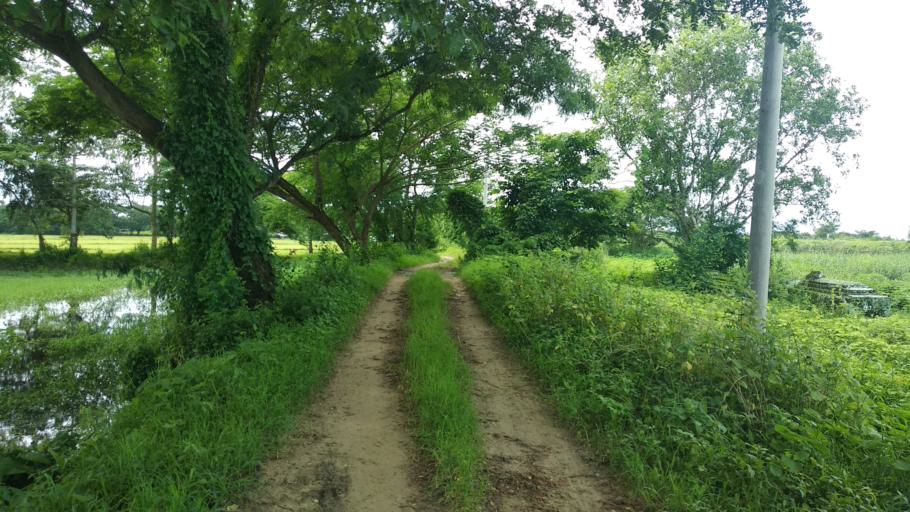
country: MM
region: Yangon
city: Kanbe
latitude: 16.8767
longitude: 95.9766
